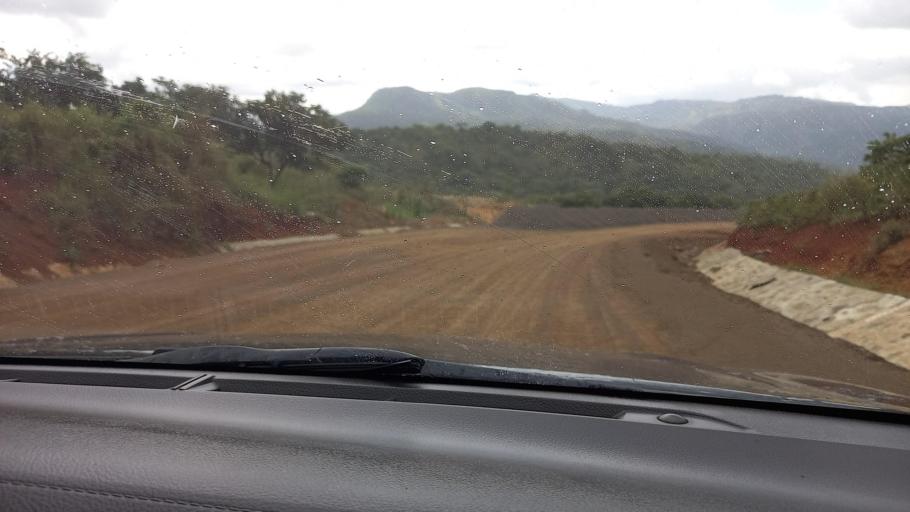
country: ET
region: Southern Nations, Nationalities, and People's Region
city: Mizan Teferi
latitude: 6.1823
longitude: 35.6928
